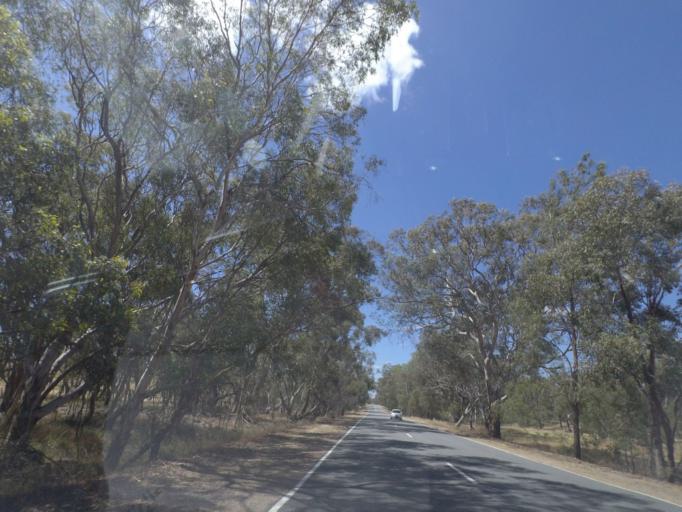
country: AU
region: Victoria
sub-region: Wangaratta
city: Wangaratta
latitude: -36.4467
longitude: 146.2411
